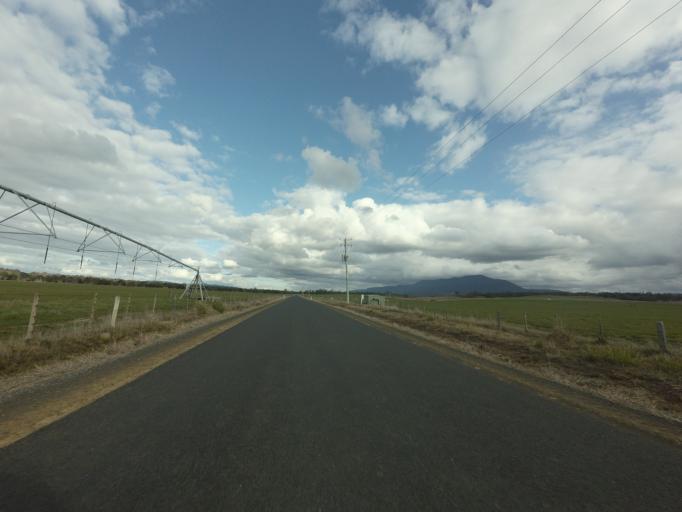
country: AU
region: Tasmania
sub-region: Northern Midlands
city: Longford
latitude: -41.8242
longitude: 147.2038
